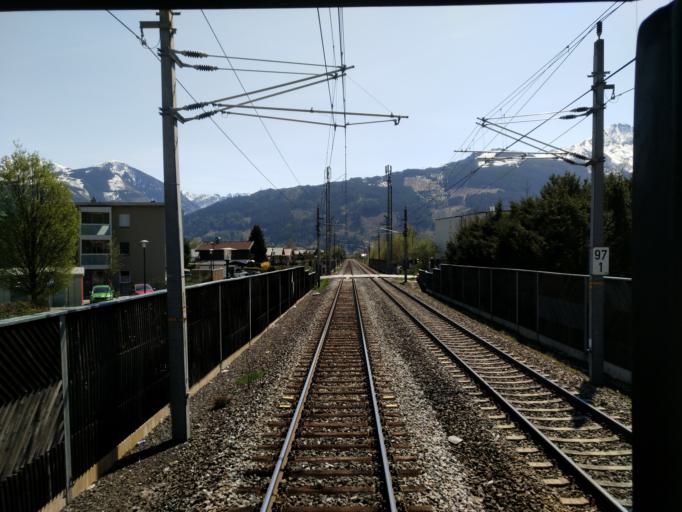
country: AT
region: Salzburg
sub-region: Politischer Bezirk Zell am See
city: Zell am See
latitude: 47.3012
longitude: 12.7964
